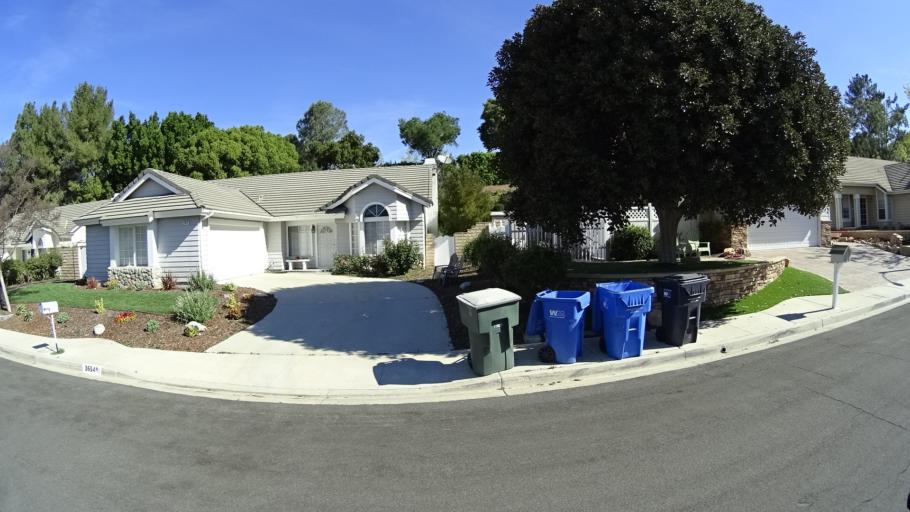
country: US
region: California
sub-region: Ventura County
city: Moorpark
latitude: 34.2295
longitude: -118.8641
